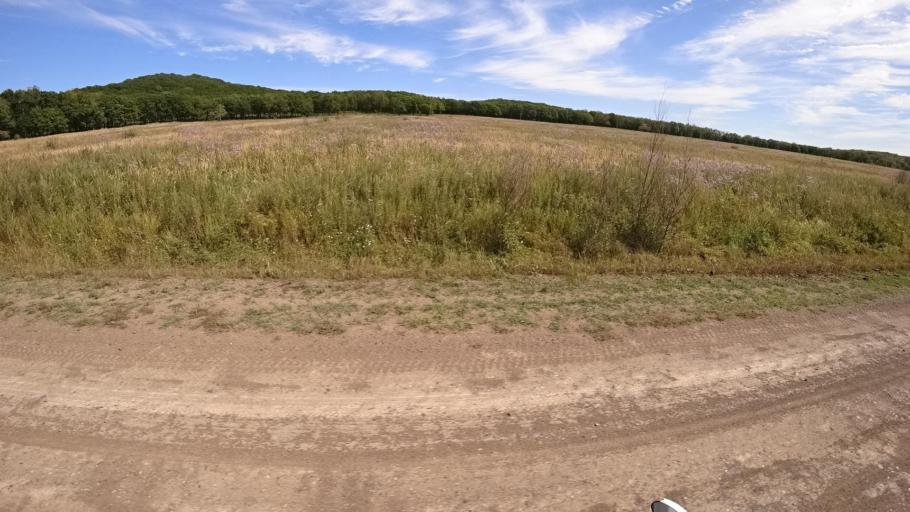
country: RU
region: Primorskiy
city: Yakovlevka
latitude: 44.7269
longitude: 133.6107
